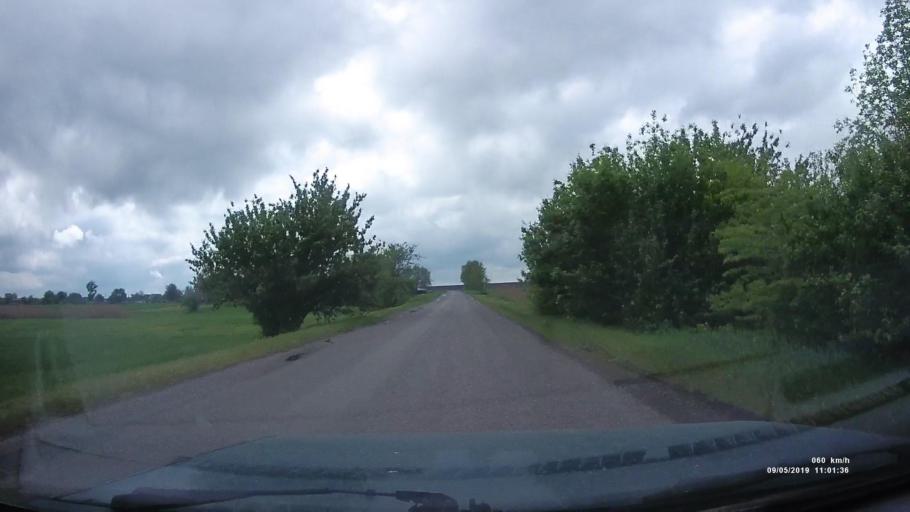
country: RU
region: Rostov
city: Peshkovo
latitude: 46.8441
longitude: 39.2136
